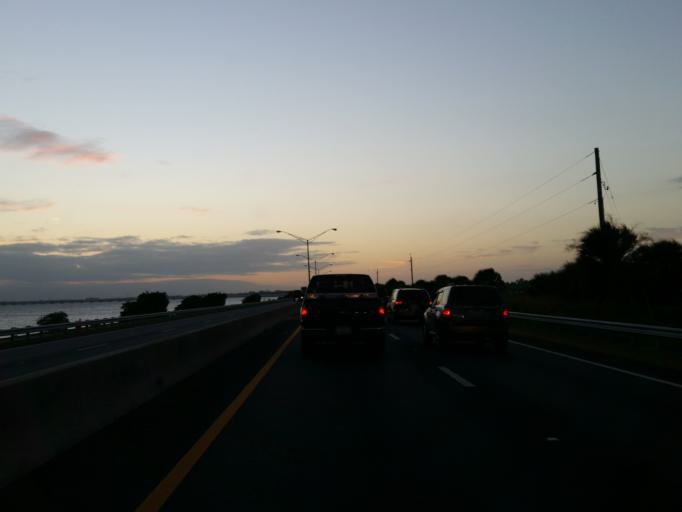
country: US
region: Florida
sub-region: Pinellas County
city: Safety Harbor
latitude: 27.9630
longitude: -82.6829
